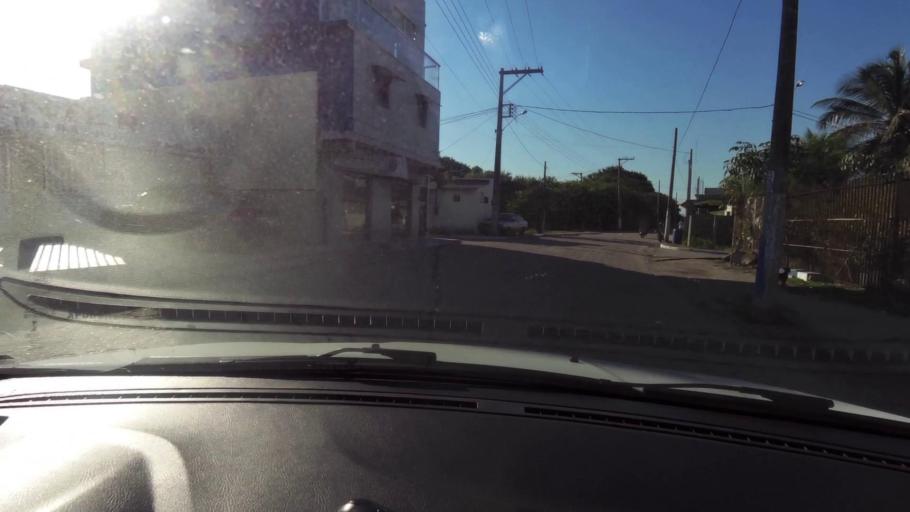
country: BR
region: Espirito Santo
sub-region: Piuma
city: Piuma
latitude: -20.7944
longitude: -40.6024
